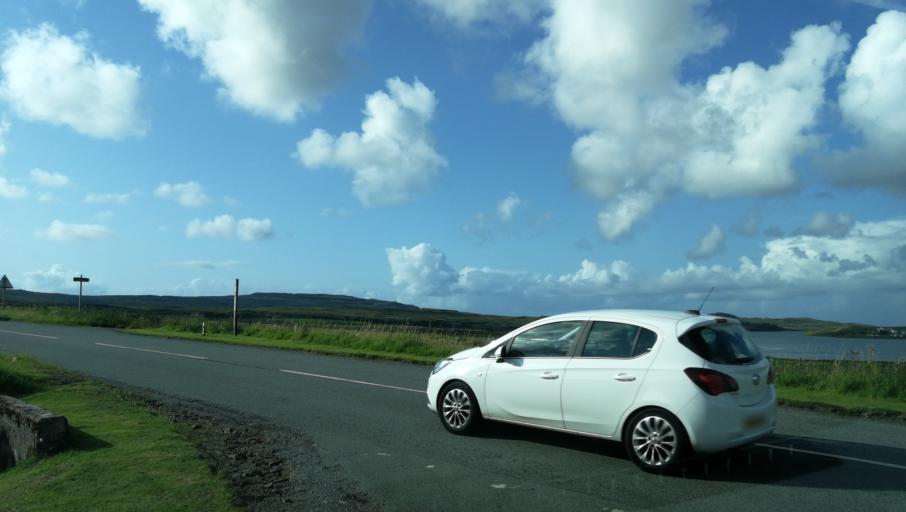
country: GB
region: Scotland
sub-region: Highland
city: Isle of Skye
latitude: 57.4710
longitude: -6.4378
